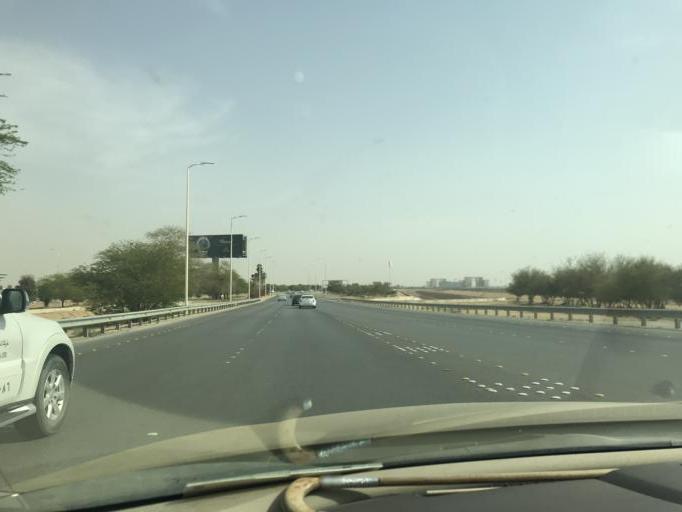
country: SA
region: Ar Riyad
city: Riyadh
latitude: 24.9425
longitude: 46.7067
